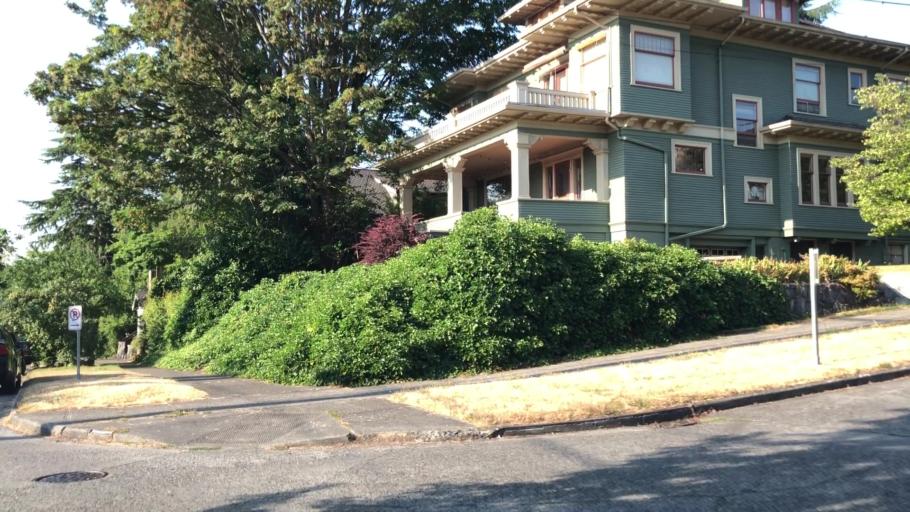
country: US
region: Washington
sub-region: King County
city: Seattle
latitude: 47.6592
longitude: -122.3339
